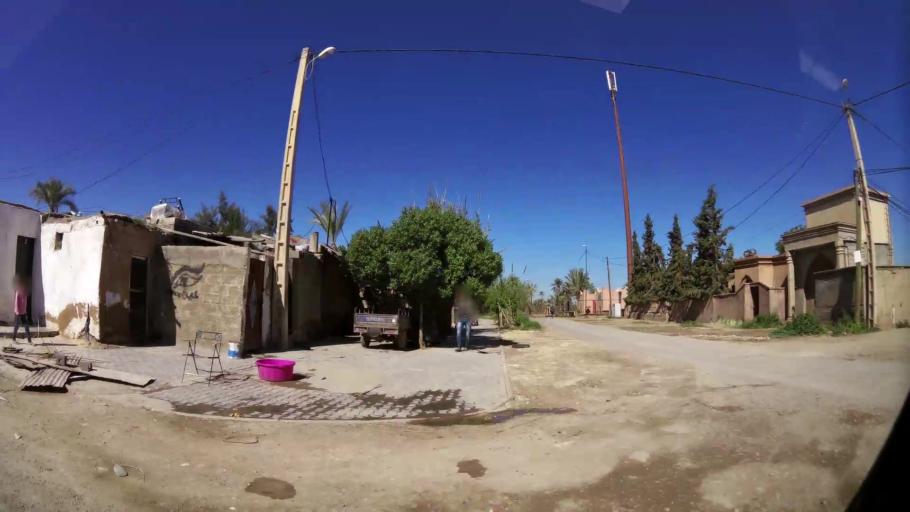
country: MA
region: Marrakech-Tensift-Al Haouz
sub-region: Marrakech
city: Marrakesh
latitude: 31.6722
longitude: -7.9566
